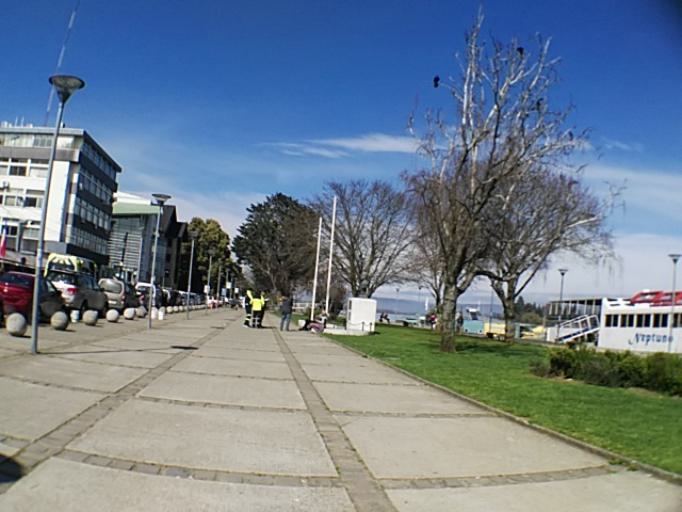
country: CL
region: Los Rios
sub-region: Provincia de Valdivia
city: Valdivia
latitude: -39.8147
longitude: -73.2487
